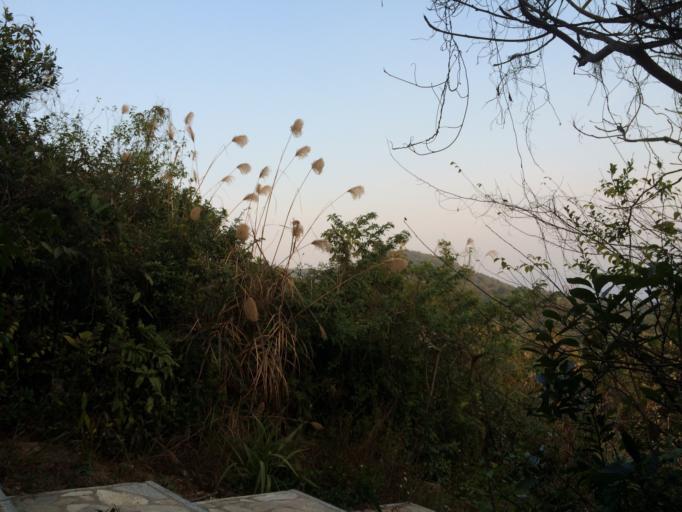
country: HK
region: Tai Po
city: Tai Po
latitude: 22.4502
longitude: 114.2199
